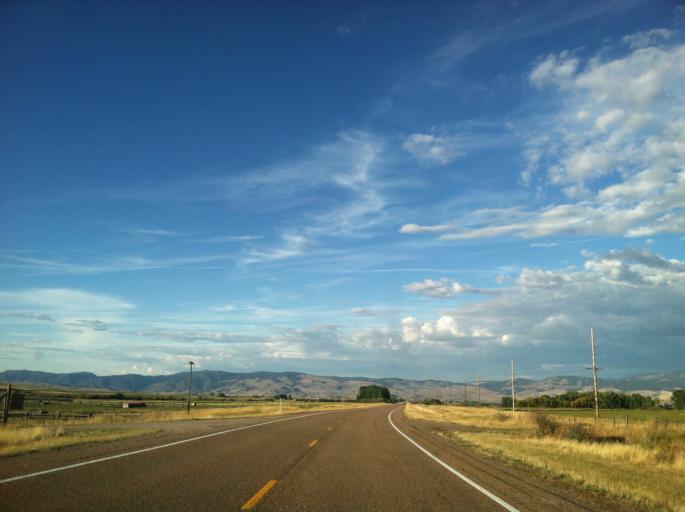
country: US
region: Montana
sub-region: Granite County
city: Philipsburg
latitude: 46.5569
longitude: -113.2158
